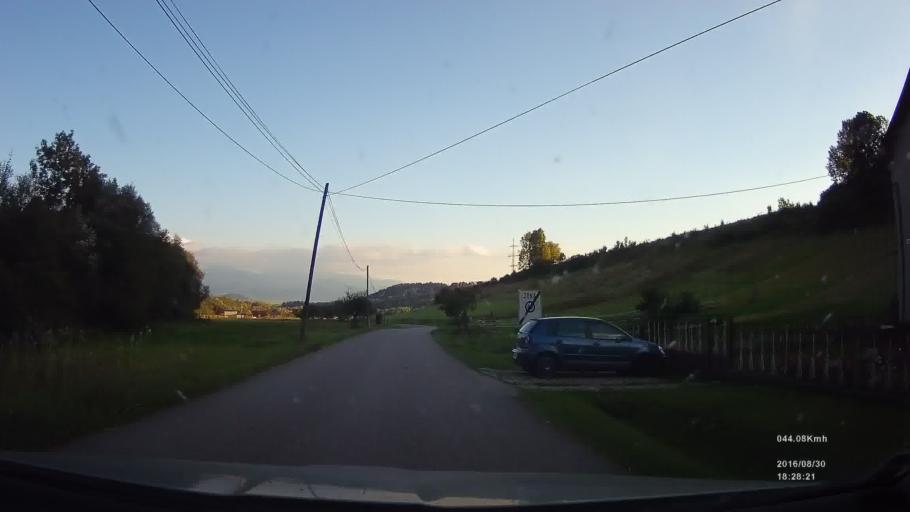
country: SK
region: Zilinsky
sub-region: Okres Liptovsky Mikulas
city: Liptovsky Mikulas
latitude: 49.1417
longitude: 19.5014
